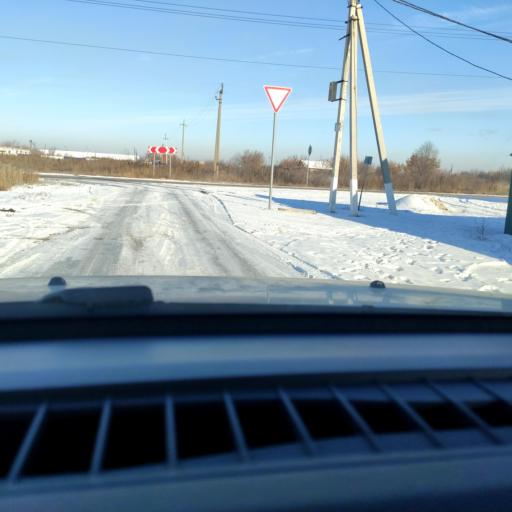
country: RU
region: Samara
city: Podstepki
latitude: 53.5187
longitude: 49.1284
